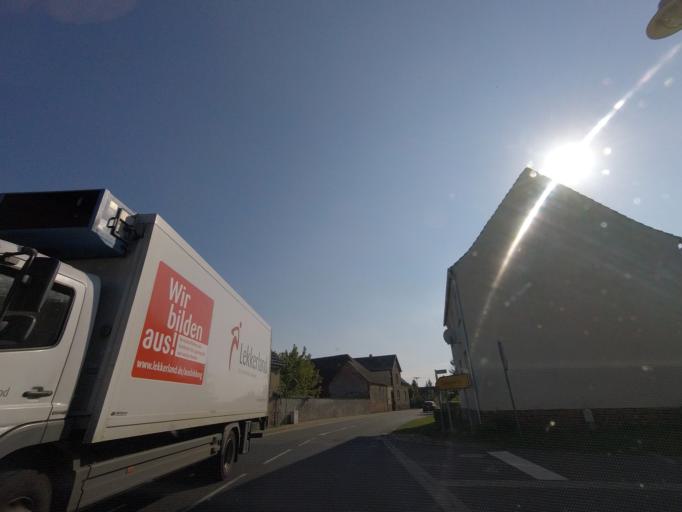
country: DE
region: Saxony-Anhalt
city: Jessen
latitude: 51.8529
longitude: 13.0253
